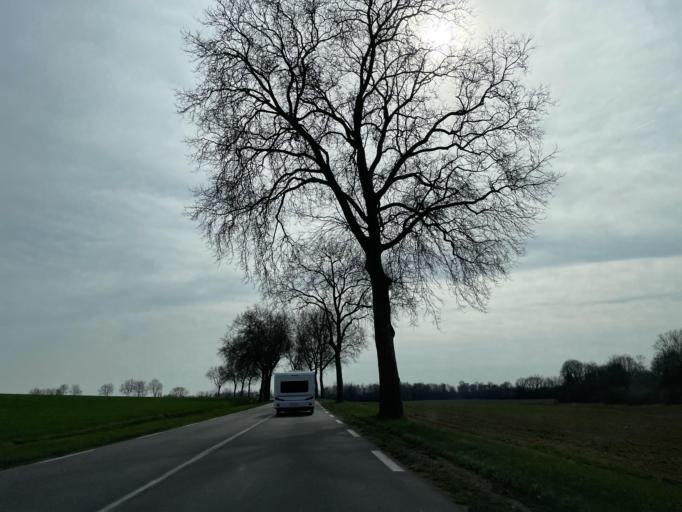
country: FR
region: Champagne-Ardenne
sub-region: Departement de l'Aube
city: Romilly-sur-Seine
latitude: 48.5099
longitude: 3.6882
